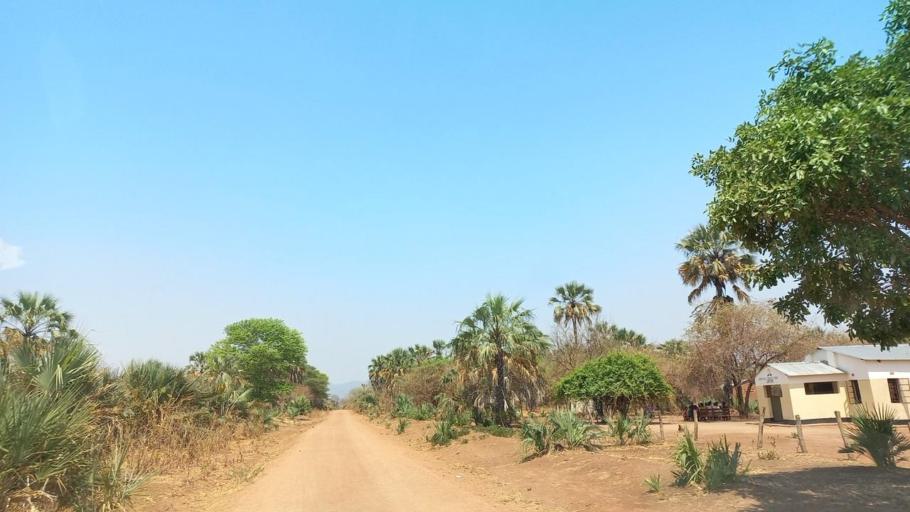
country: ZM
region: Lusaka
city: Luangwa
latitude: -15.1869
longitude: 30.2120
